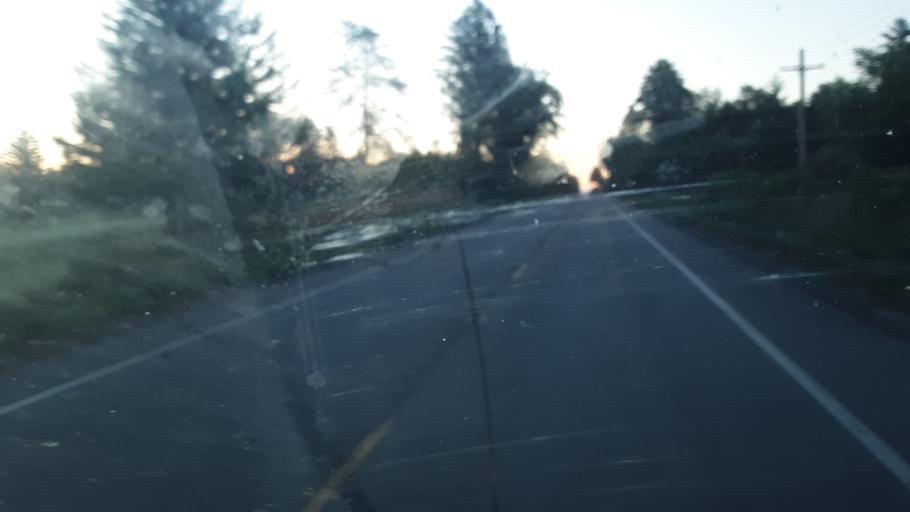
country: US
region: New York
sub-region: Saratoga County
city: Ballston Spa
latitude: 42.9987
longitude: -73.8754
